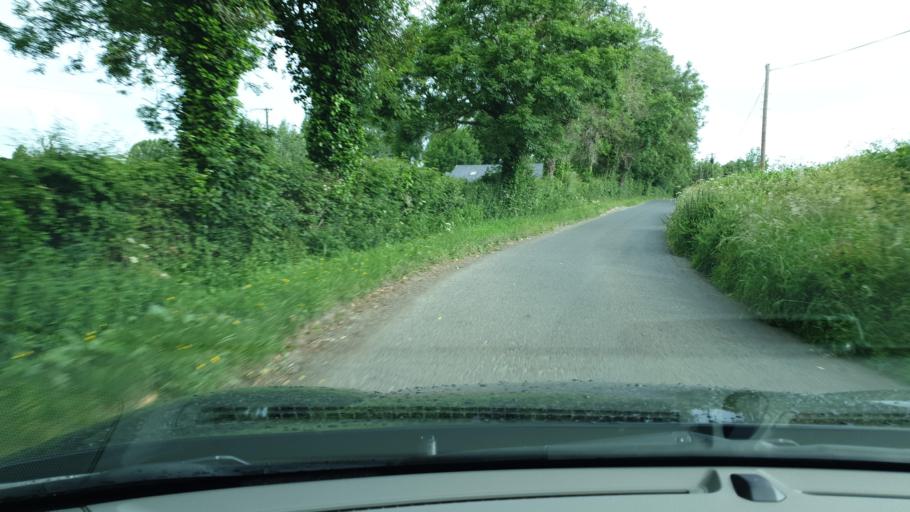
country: IE
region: Leinster
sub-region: An Mhi
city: Ashbourne
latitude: 53.5166
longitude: -6.3851
